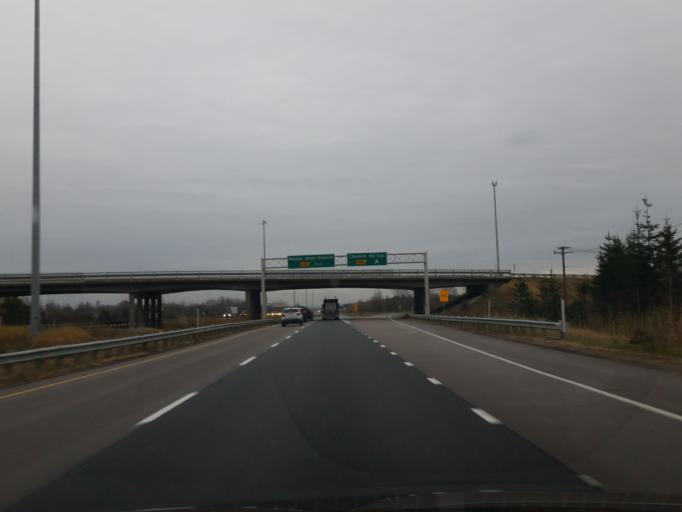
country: CA
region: Quebec
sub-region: Capitale-Nationale
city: Saint-Augustin-de-Desmaures
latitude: 46.7557
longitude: -71.4011
